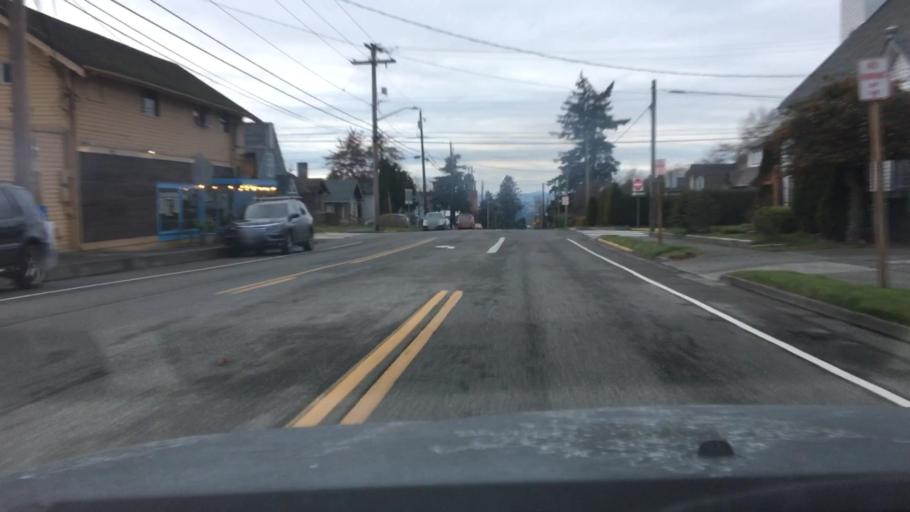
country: US
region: Washington
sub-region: Skagit County
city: Mount Vernon
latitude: 48.4211
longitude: -122.3281
